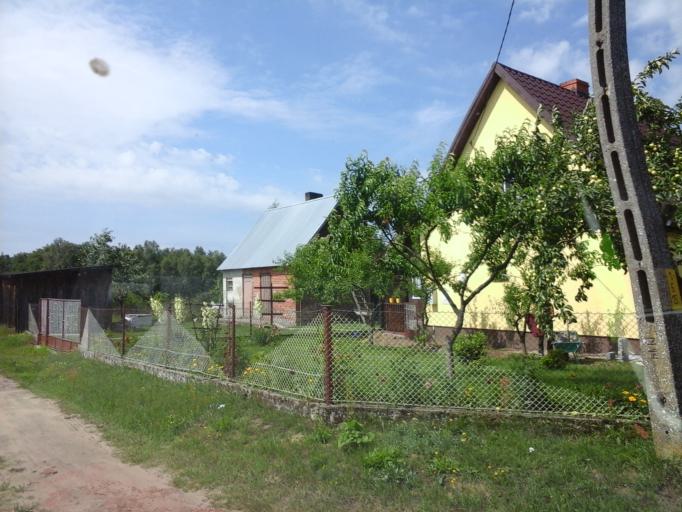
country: PL
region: West Pomeranian Voivodeship
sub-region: Powiat choszczenski
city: Bierzwnik
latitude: 53.0267
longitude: 15.6857
